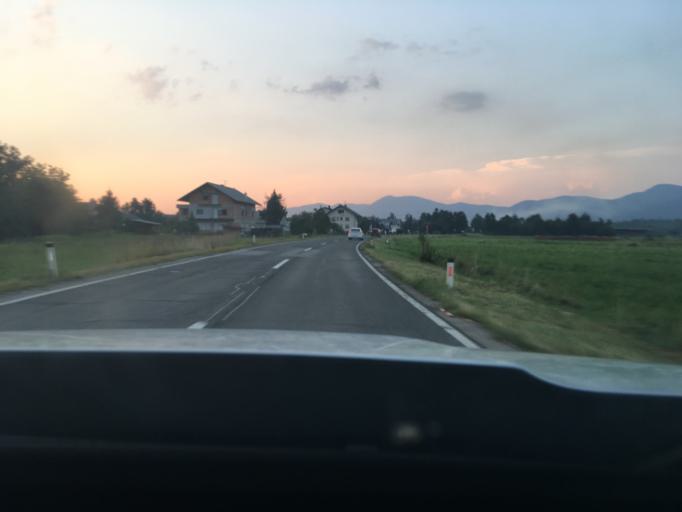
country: SI
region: Ribnica
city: Ribnica
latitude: 45.7040
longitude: 14.7575
